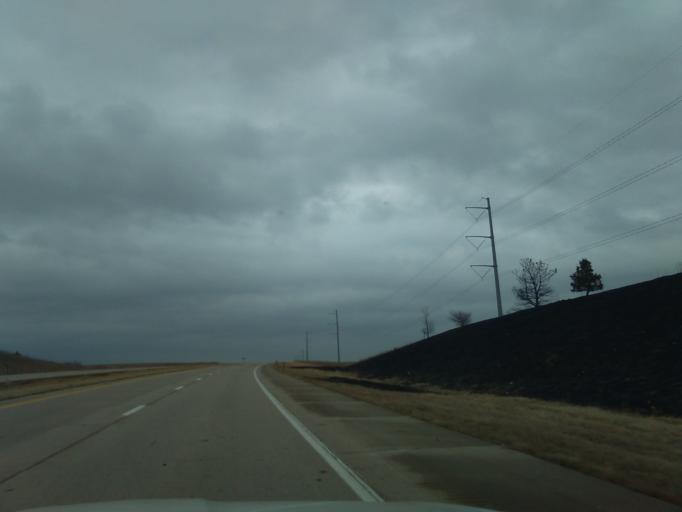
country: US
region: Nebraska
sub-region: Otoe County
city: Syracuse
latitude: 40.6754
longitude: -96.0751
